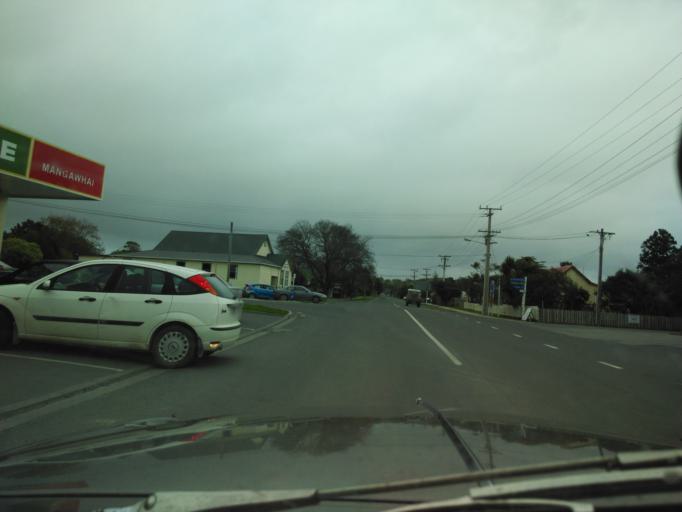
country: NZ
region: Auckland
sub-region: Auckland
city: Wellsford
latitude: -36.1260
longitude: 174.5750
